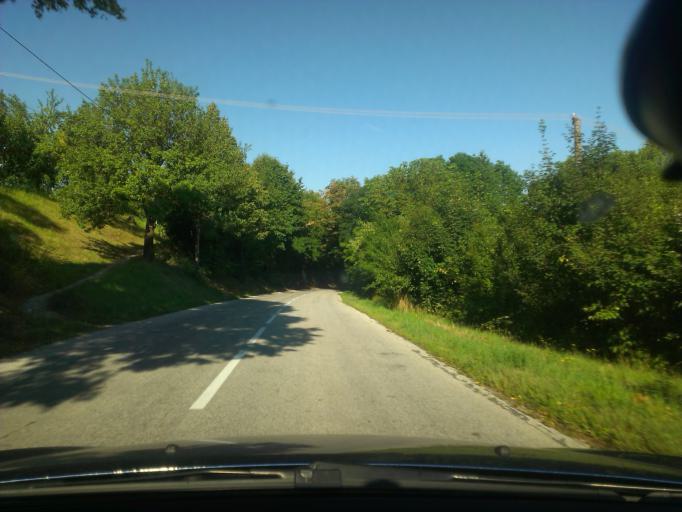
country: SK
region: Trenciansky
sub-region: Okres Myjava
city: Myjava
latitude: 48.7557
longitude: 17.5712
